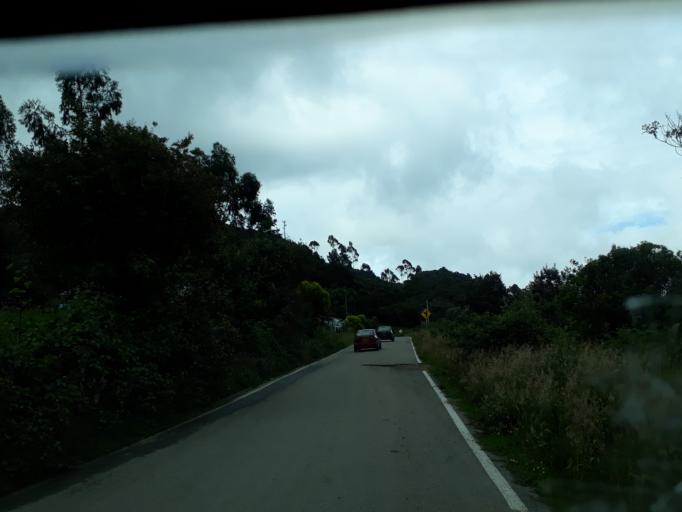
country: CO
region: Cundinamarca
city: La Mesa
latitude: 5.2053
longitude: -73.9027
